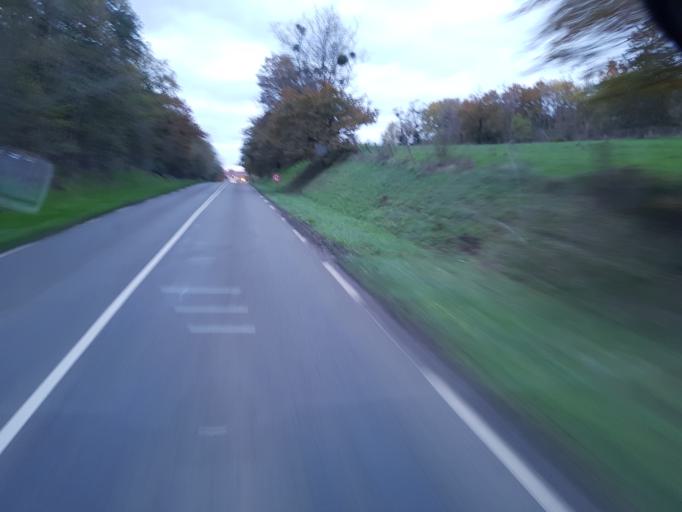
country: FR
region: Picardie
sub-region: Departement de l'Aisne
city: Coincy
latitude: 49.1446
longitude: 3.3871
